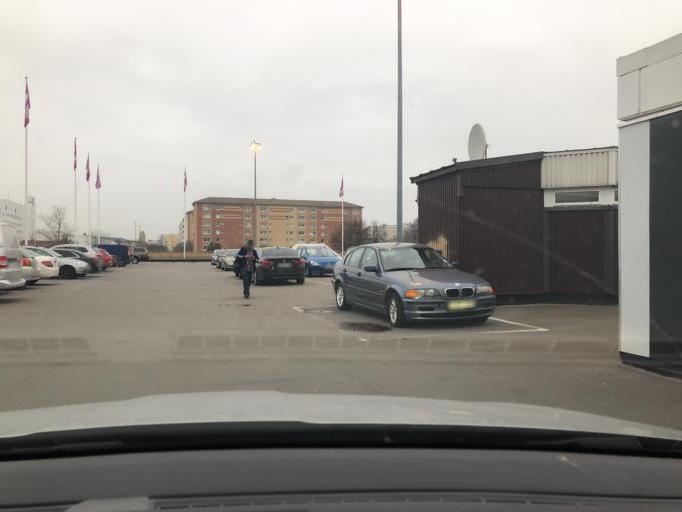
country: SE
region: Stockholm
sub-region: Botkyrka Kommun
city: Eriksberg
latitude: 59.2447
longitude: 17.8255
